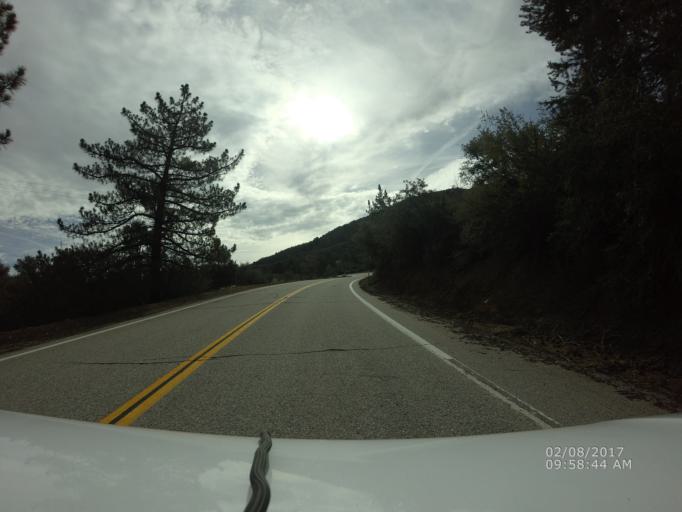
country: US
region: California
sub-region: San Bernardino County
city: Pinon Hills
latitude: 34.4099
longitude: -117.7705
